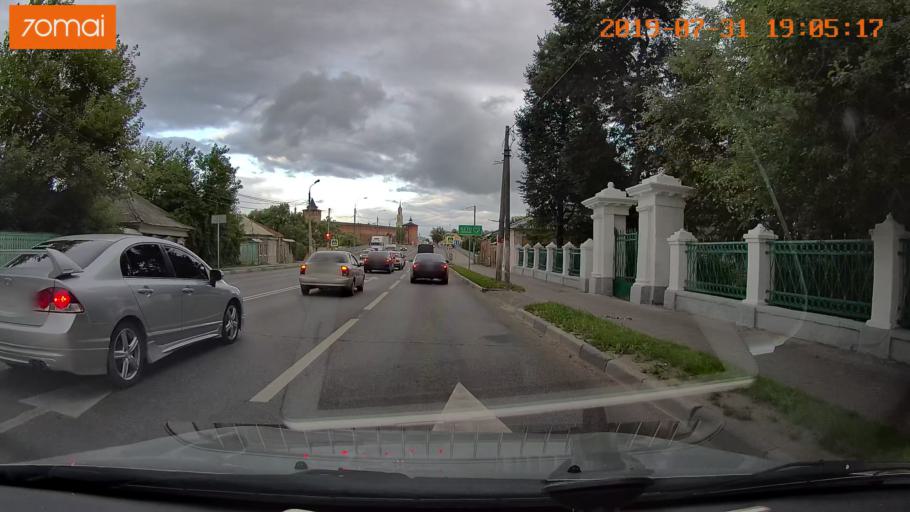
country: RU
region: Moskovskaya
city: Raduzhnyy
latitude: 55.1061
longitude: 38.7461
